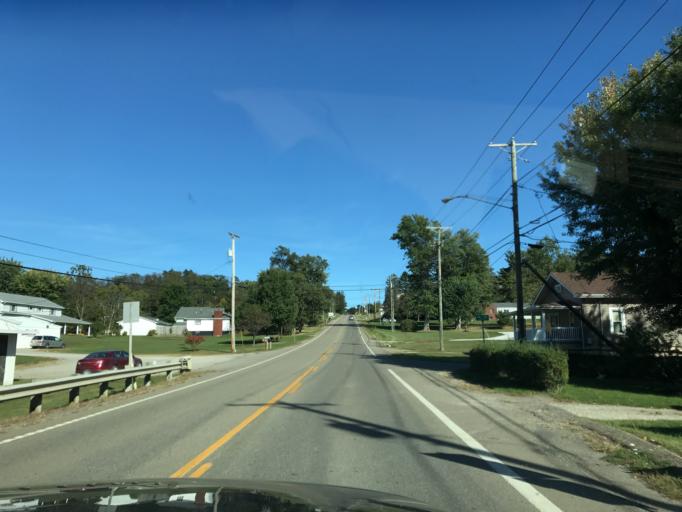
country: US
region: Ohio
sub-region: Belmont County
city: Saint Clairsville
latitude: 40.0729
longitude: -80.9524
